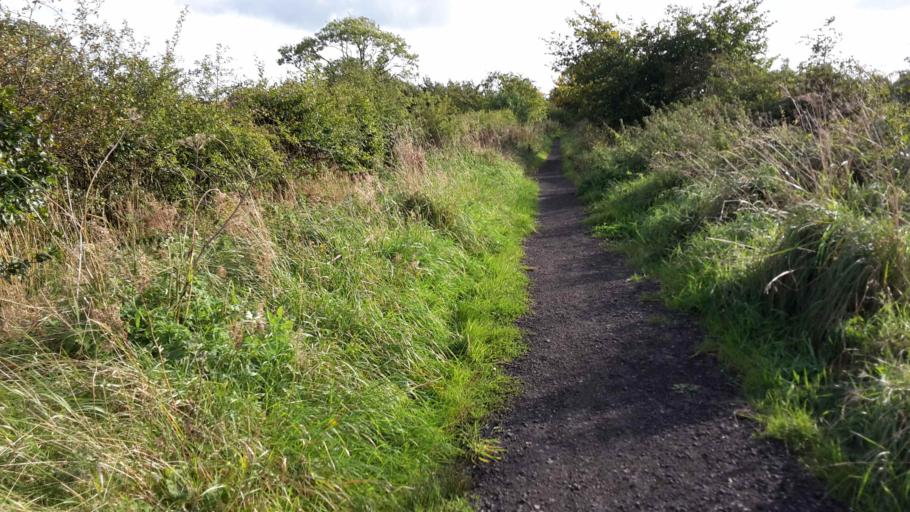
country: GB
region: Scotland
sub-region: South Lanarkshire
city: Carluke
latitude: 55.7194
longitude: -3.8275
